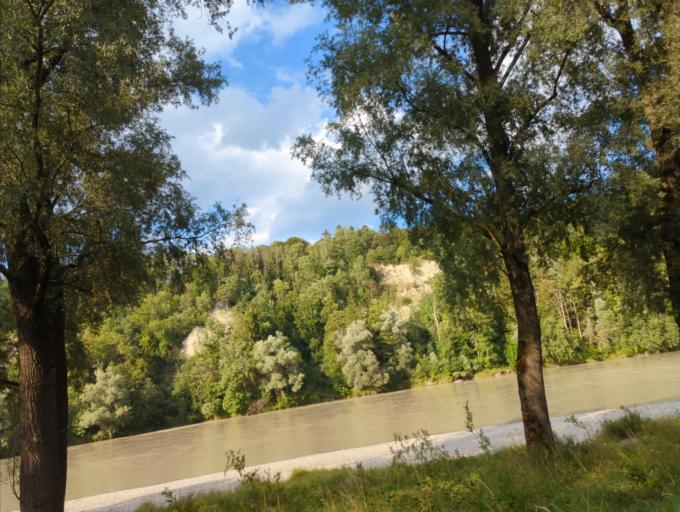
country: DE
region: Bavaria
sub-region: Upper Bavaria
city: Wasserburg am Inn
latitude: 48.0644
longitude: 12.2361
